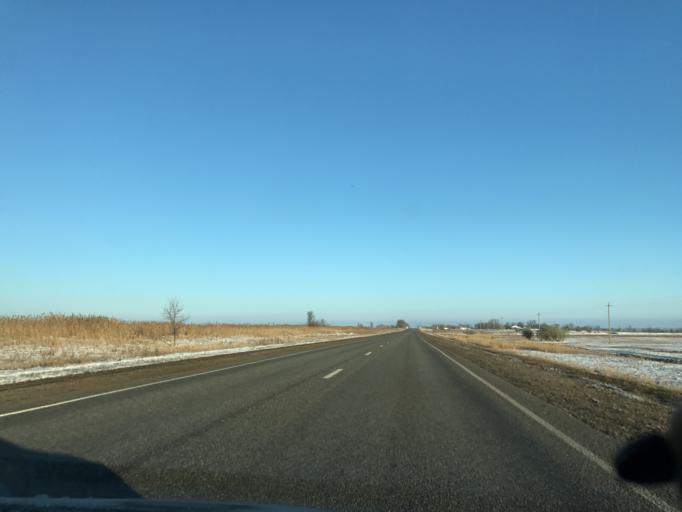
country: RU
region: Stavropol'skiy
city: Bezopasnoye
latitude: 45.5812
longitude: 41.9469
